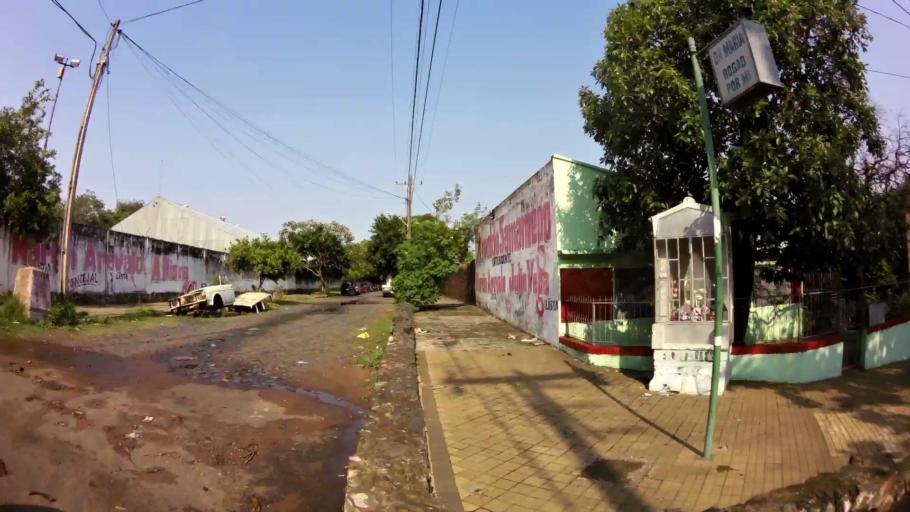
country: PY
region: Presidente Hayes
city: Nanawa
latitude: -25.2828
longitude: -57.6646
